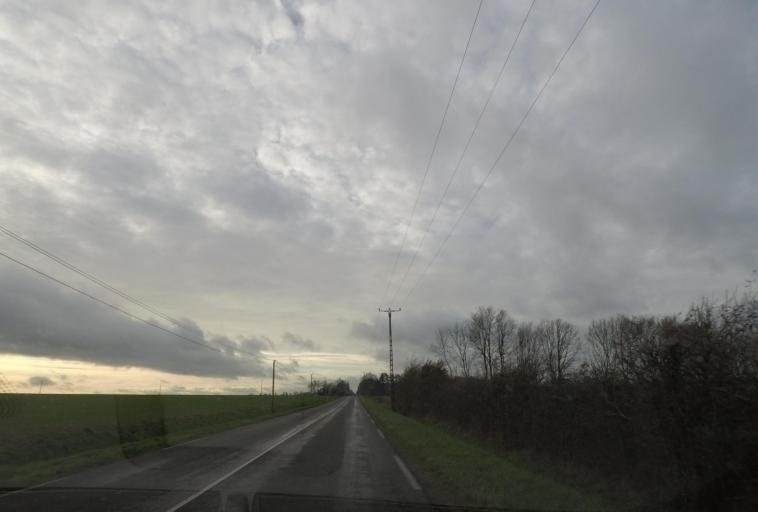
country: FR
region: Pays de la Loire
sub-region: Departement de la Sarthe
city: Saint-Calais
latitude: 47.9518
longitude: 0.7538
